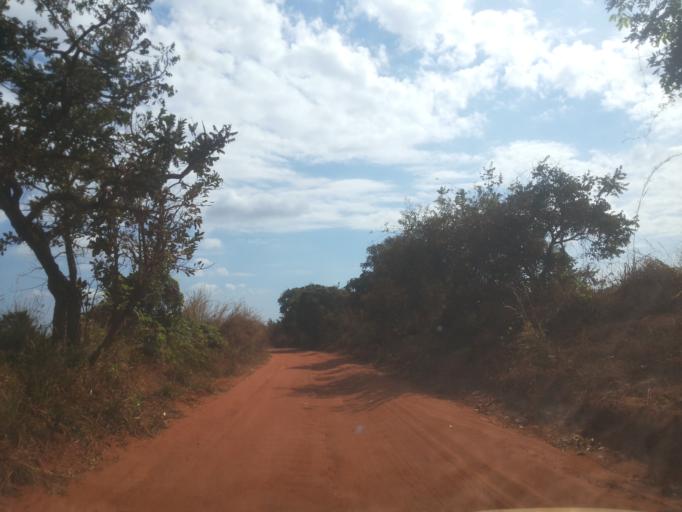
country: BR
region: Minas Gerais
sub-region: Ituiutaba
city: Ituiutaba
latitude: -19.0078
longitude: -49.4027
